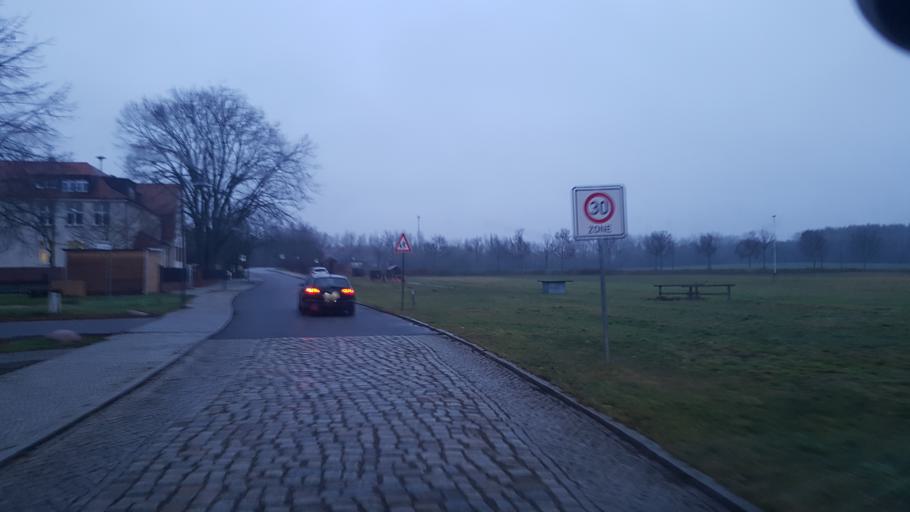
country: DE
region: Brandenburg
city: Ludwigsfelde
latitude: 52.3161
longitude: 13.1999
